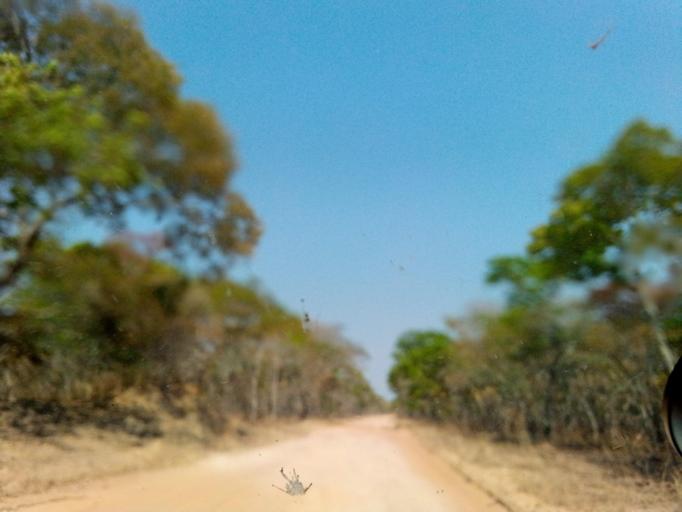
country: ZM
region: Northern
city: Mpika
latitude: -12.2421
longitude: 30.8391
